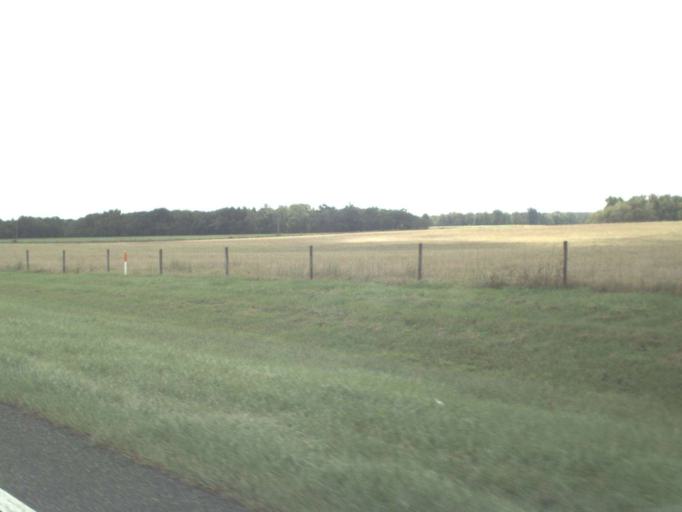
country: US
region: Florida
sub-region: Jackson County
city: Marianna
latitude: 30.8628
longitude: -85.3563
